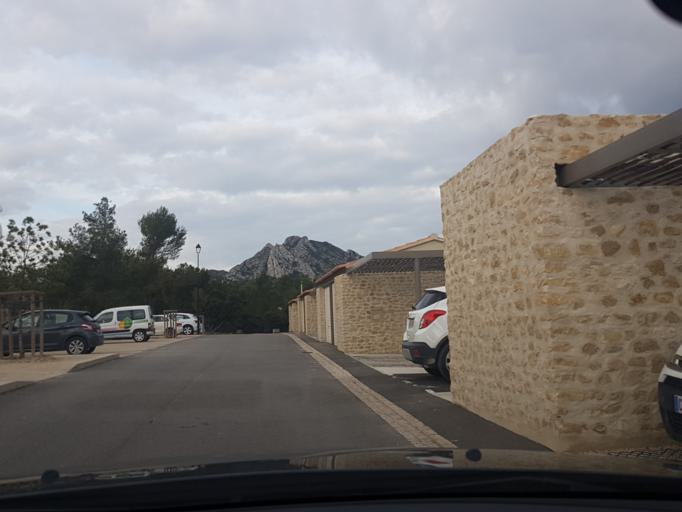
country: FR
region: Provence-Alpes-Cote d'Azur
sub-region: Departement des Bouches-du-Rhone
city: Eygalieres
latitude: 43.7541
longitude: 4.9522
